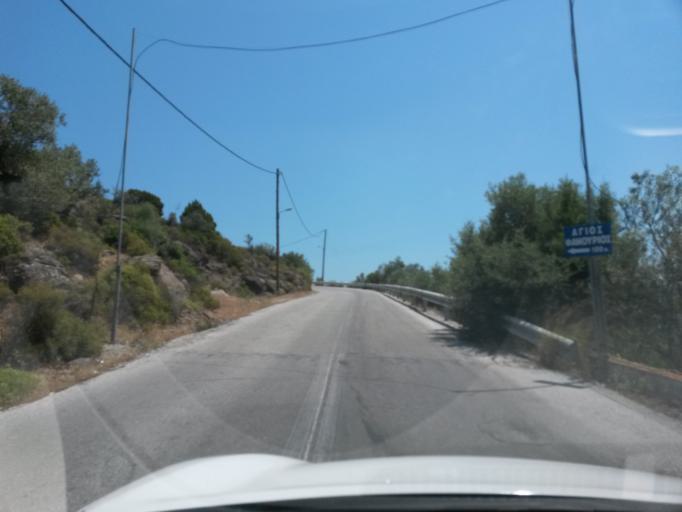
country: GR
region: North Aegean
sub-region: Nomos Lesvou
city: Mantamados
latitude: 39.2463
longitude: 26.4277
